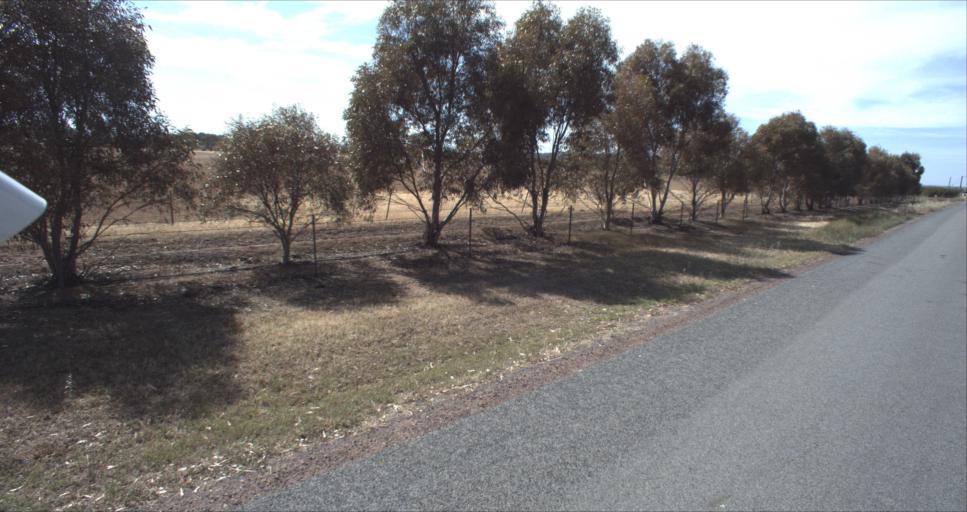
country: AU
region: New South Wales
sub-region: Leeton
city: Leeton
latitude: -34.5721
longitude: 146.4662
